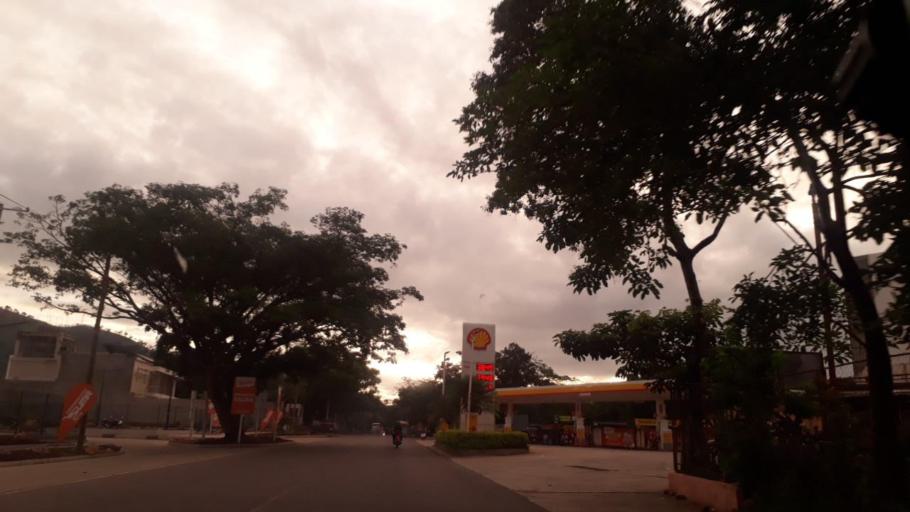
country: GT
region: Jutiapa
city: Jutiapa
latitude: 14.2998
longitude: -89.8946
